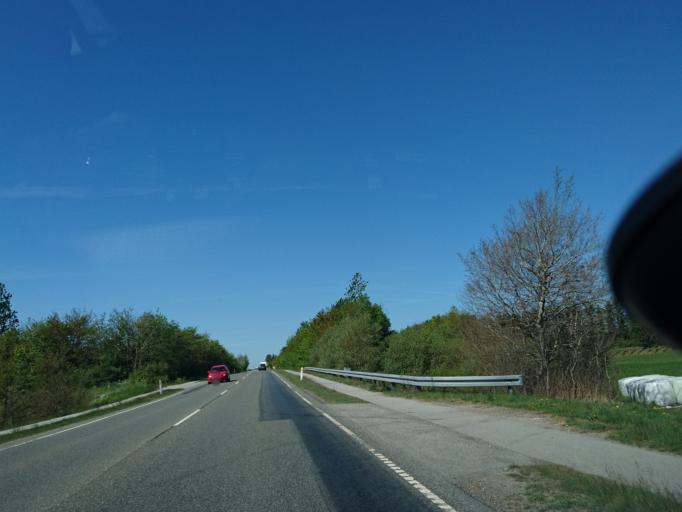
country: DK
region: North Denmark
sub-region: Hjorring Kommune
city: Tars
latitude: 57.4565
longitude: 10.0753
